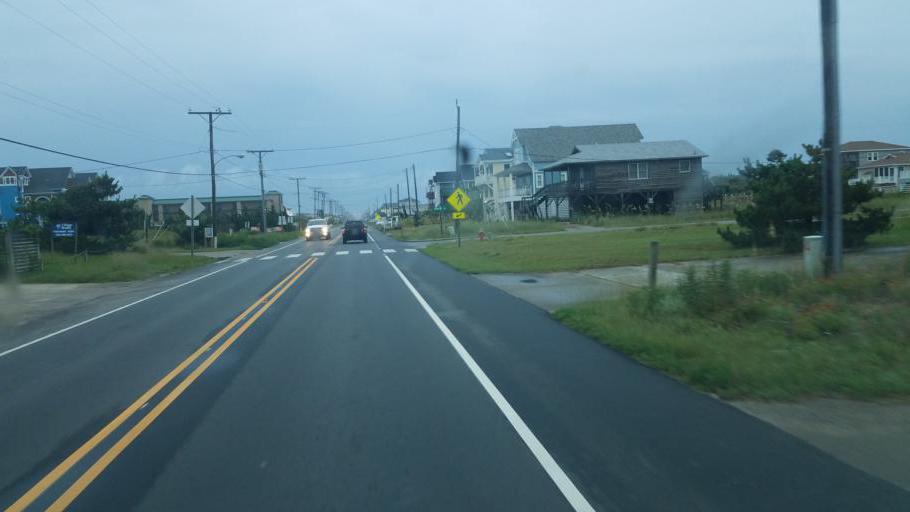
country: US
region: North Carolina
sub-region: Dare County
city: Kill Devil Hills
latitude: 36.0190
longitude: -75.6603
